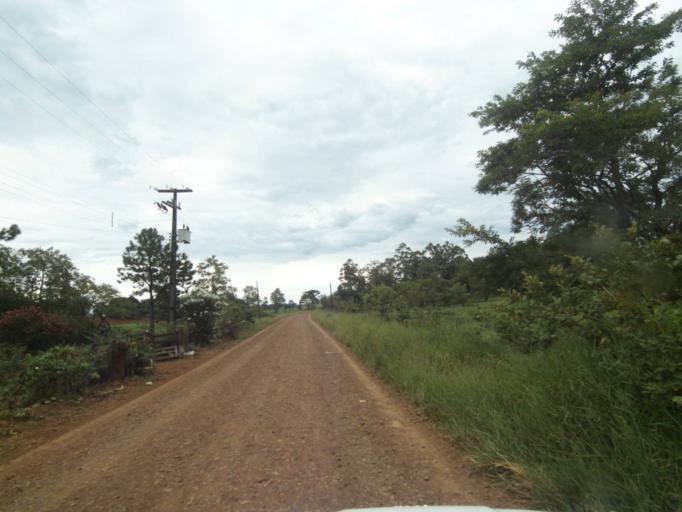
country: BR
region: Parana
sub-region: Guaraniacu
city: Guaraniacu
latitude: -24.9098
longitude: -52.9356
